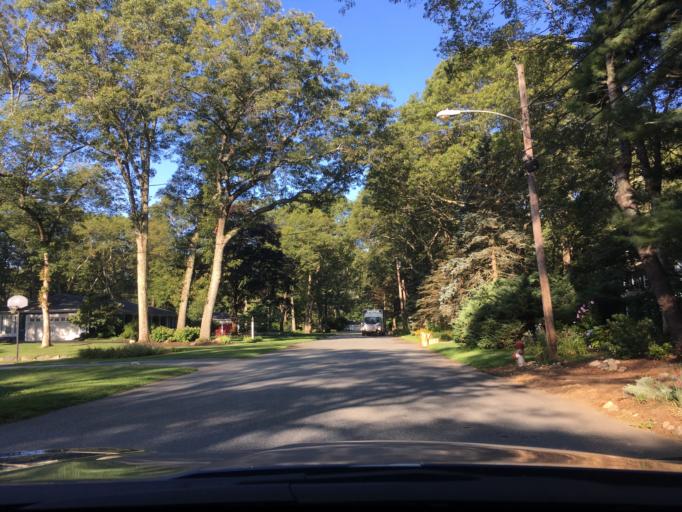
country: US
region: Rhode Island
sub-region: Kent County
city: East Greenwich
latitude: 41.6417
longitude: -71.4820
